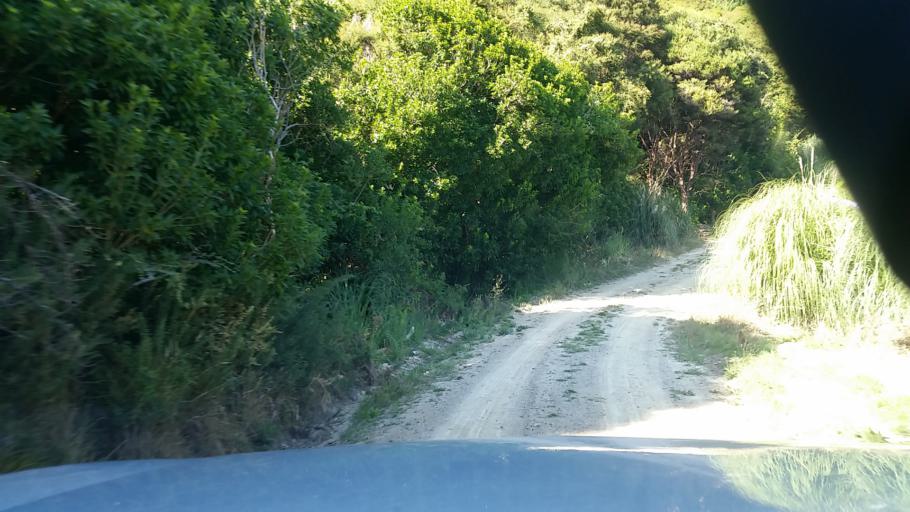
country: NZ
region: Marlborough
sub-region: Marlborough District
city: Picton
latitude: -41.3149
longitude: 174.1748
